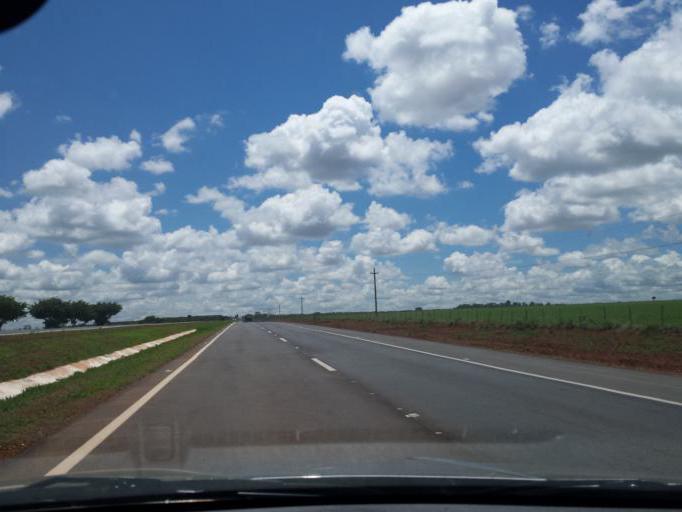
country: BR
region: Goias
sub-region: Cristalina
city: Cristalina
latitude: -16.7073
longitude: -47.6850
